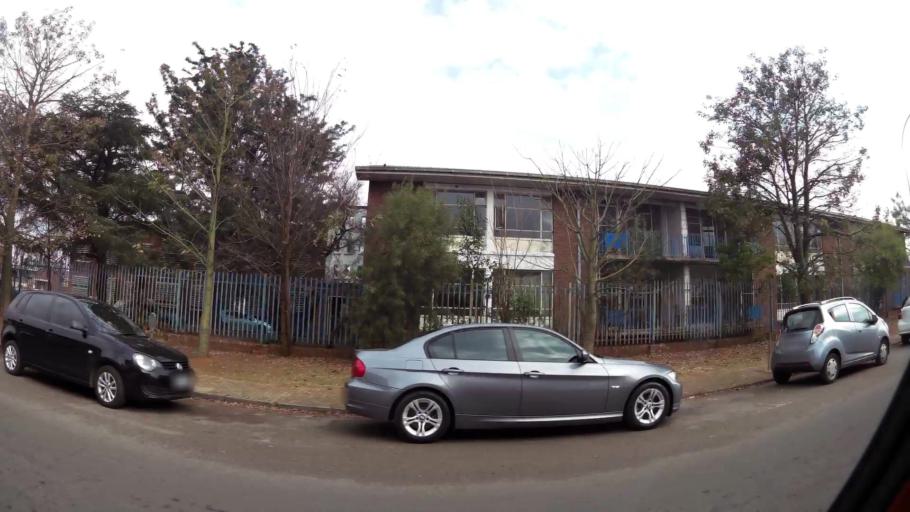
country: ZA
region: Gauteng
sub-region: Sedibeng District Municipality
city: Vanderbijlpark
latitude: -26.6986
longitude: 27.8335
